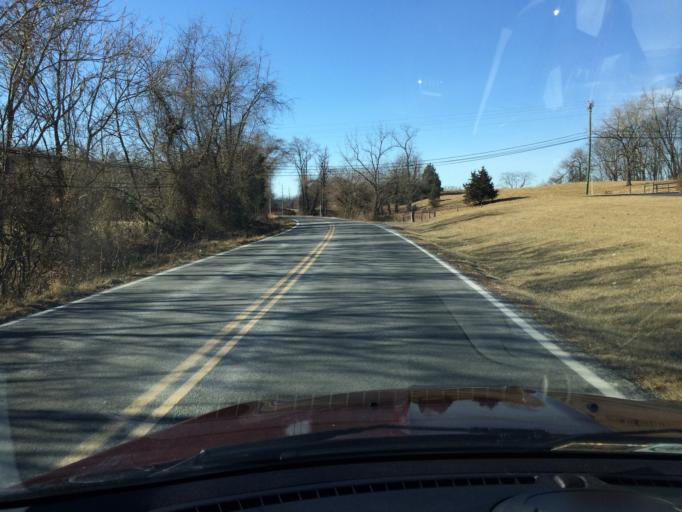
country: US
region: Virginia
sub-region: Rockingham County
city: Dayton
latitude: 38.4209
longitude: -78.9073
